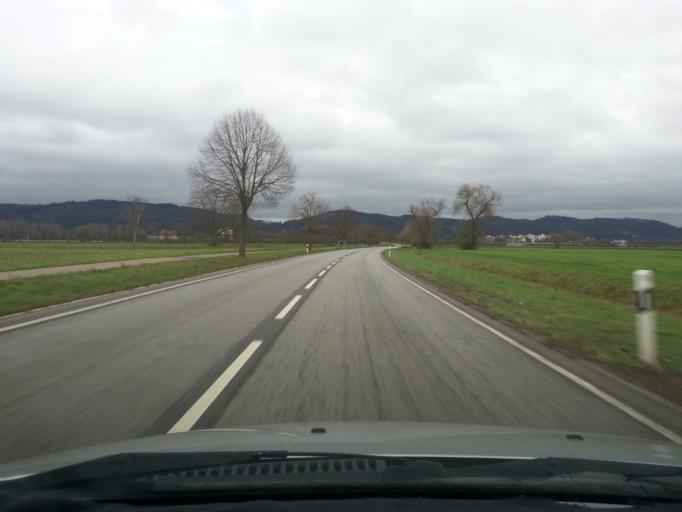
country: DE
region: Baden-Wuerttemberg
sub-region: Karlsruhe Region
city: Hemsbach
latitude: 49.5947
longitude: 8.6201
